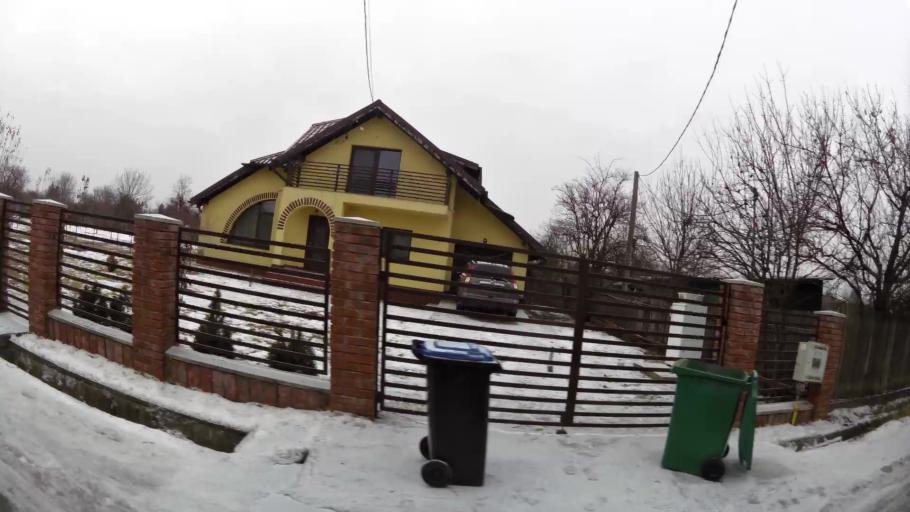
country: RO
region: Dambovita
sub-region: Comuna Aninoasa
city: Viforata
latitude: 44.9422
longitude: 25.4739
